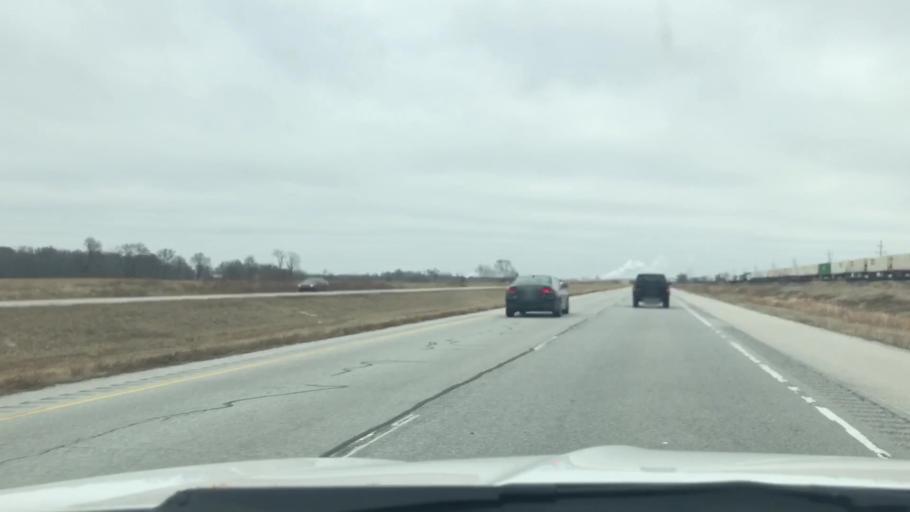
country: US
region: Indiana
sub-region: Cass County
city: Georgetown
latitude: 40.6843
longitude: -86.4932
